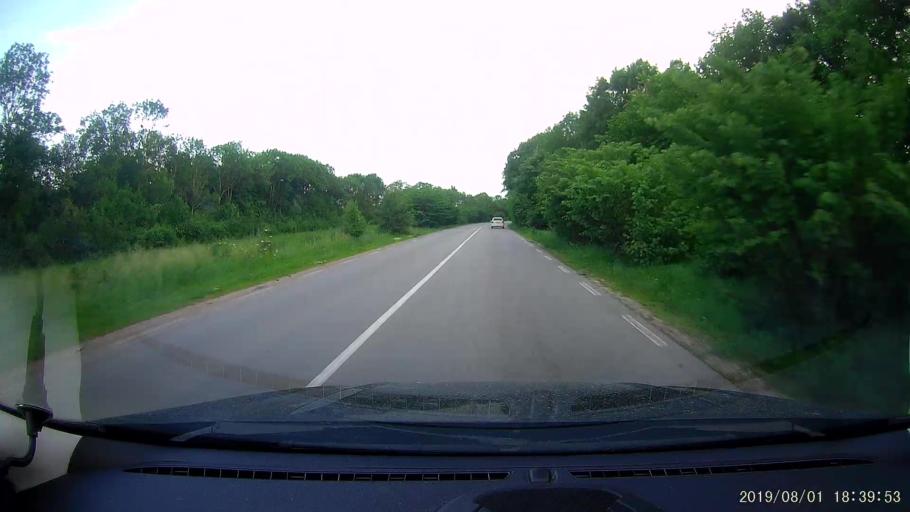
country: BG
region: Shumen
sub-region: Obshtina Khitrino
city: Gara Khitrino
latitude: 43.3766
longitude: 26.9191
